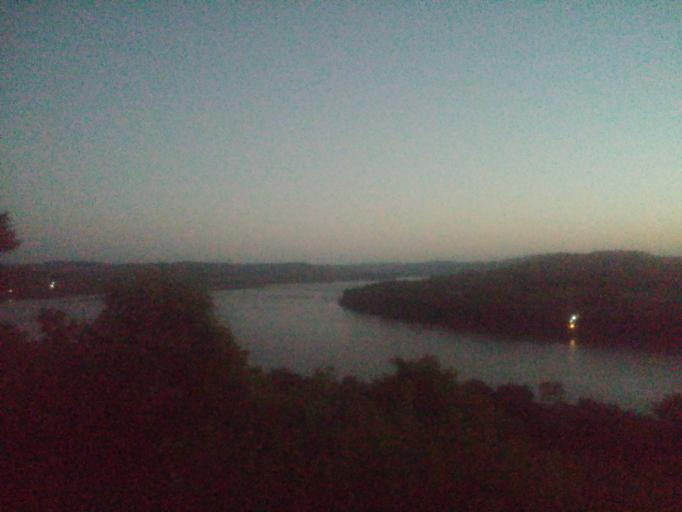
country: AR
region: Misiones
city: Alba Posse
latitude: -27.5259
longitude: -54.8060
